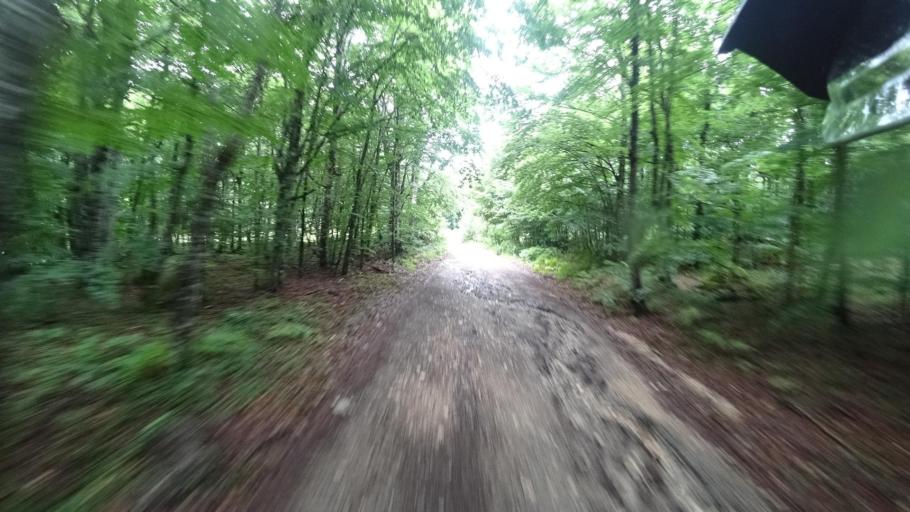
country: HR
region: Karlovacka
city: Plaski
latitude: 44.9050
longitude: 15.4167
